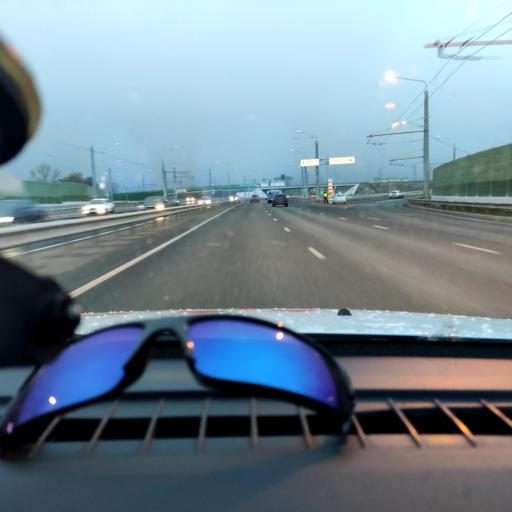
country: RU
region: Samara
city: Samara
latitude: 53.1626
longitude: 50.0877
